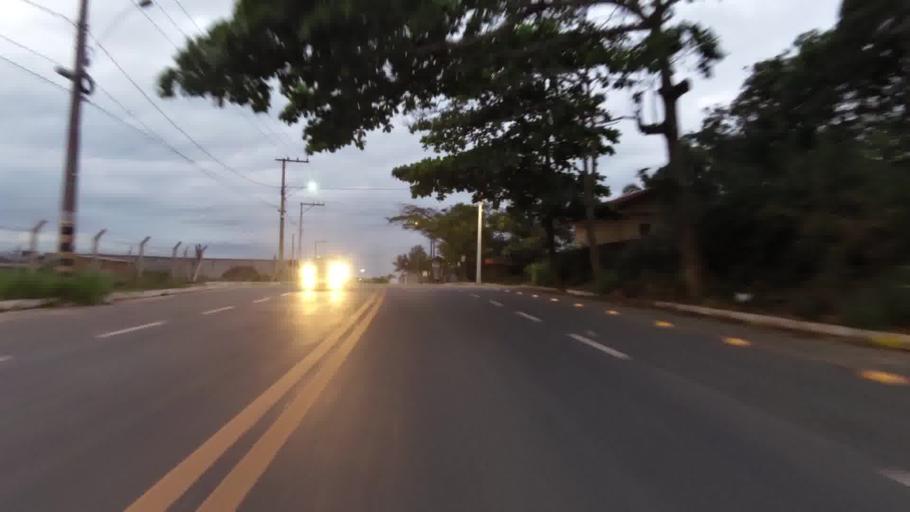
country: BR
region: Espirito Santo
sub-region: Piuma
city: Piuma
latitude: -20.8203
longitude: -40.6172
